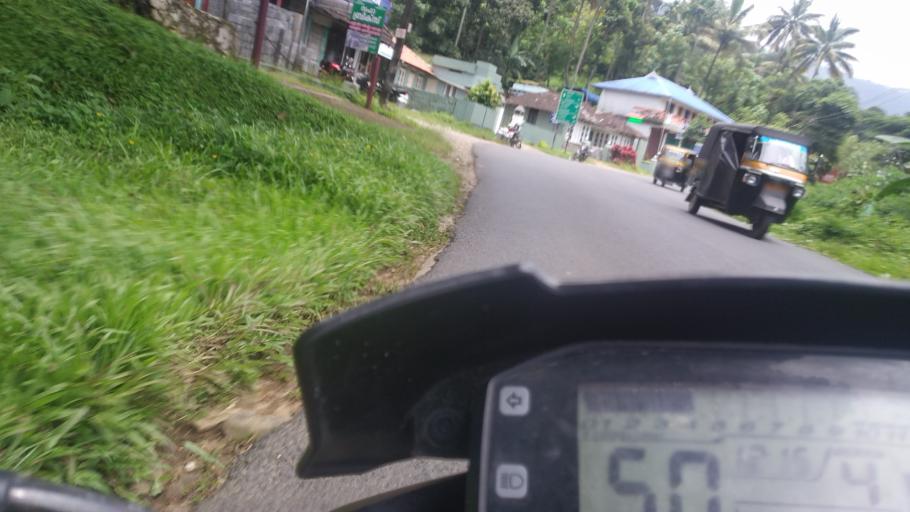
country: IN
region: Kerala
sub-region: Idukki
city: Munnar
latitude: 10.0126
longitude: 77.0099
